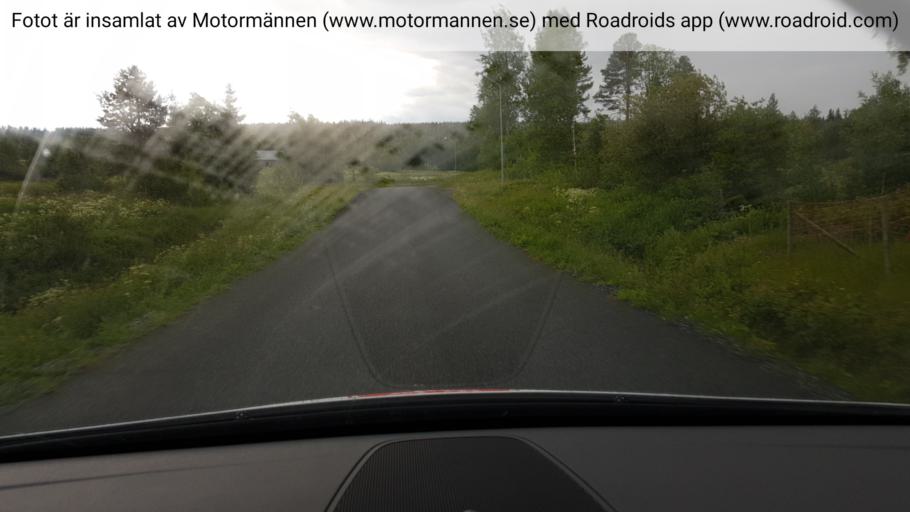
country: SE
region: Jaemtland
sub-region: OEstersunds Kommun
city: Lit
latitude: 63.5652
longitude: 14.9506
